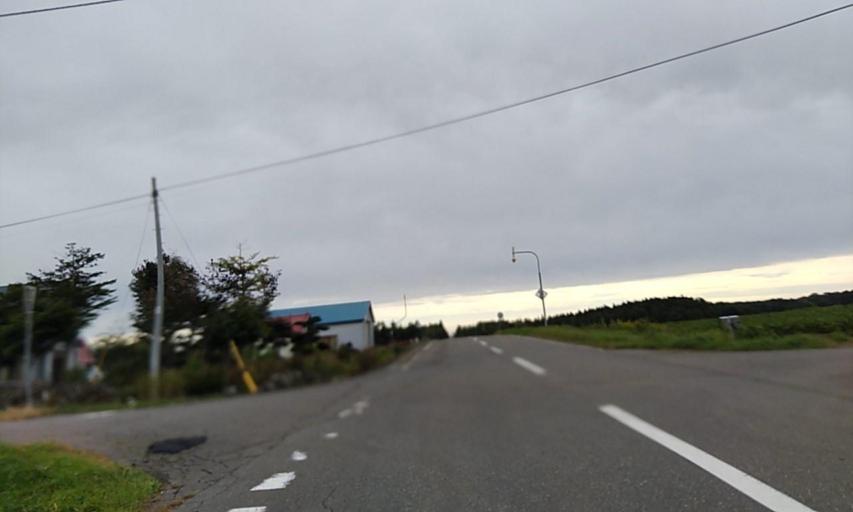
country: JP
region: Hokkaido
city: Obihiro
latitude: 42.6716
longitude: 143.0527
